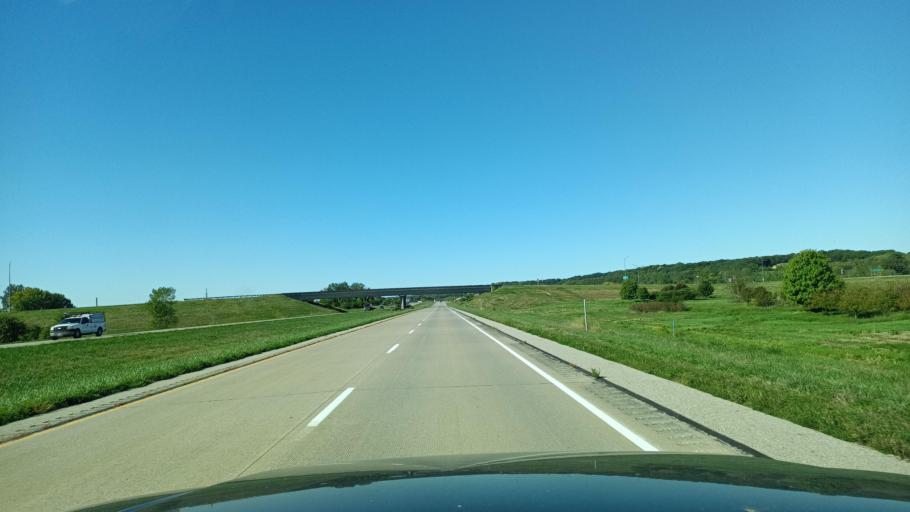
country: US
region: Illinois
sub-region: Hancock County
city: Nauvoo
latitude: 40.6275
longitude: -91.3957
